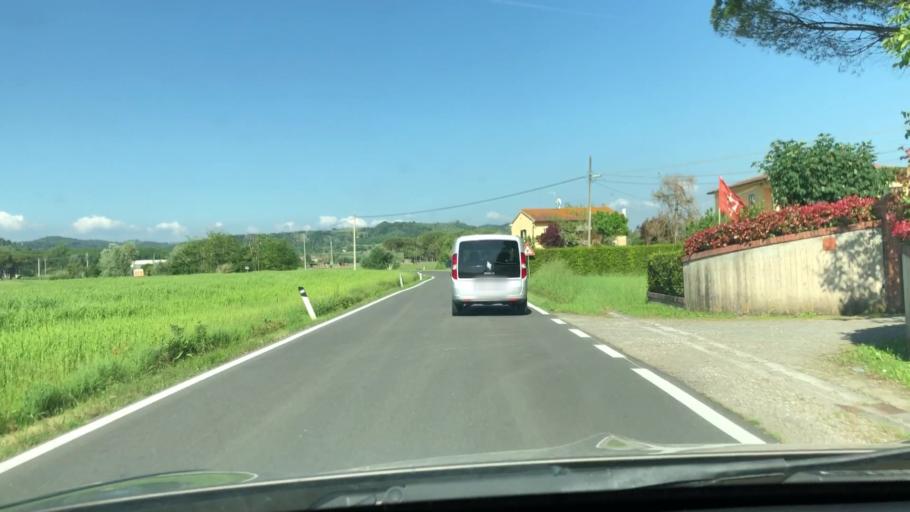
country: IT
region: Tuscany
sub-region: Province of Pisa
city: Capannoli
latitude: 43.5935
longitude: 10.6883
